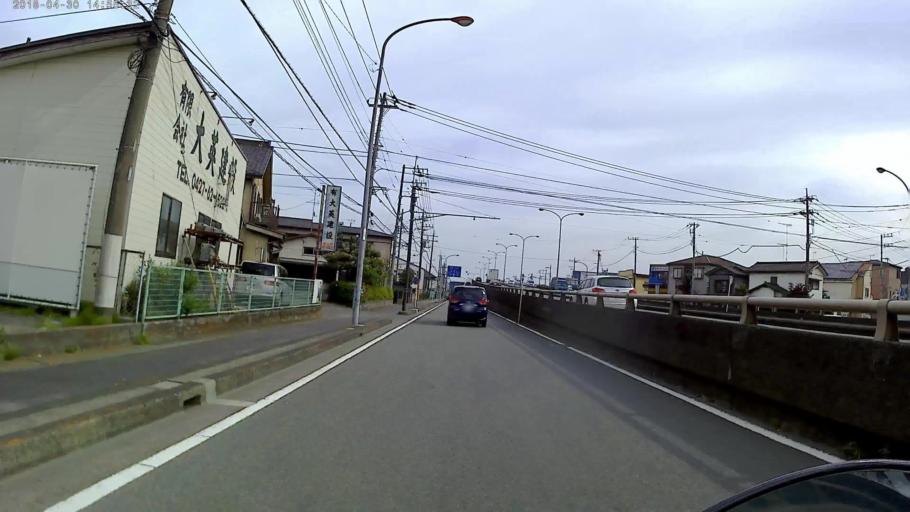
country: JP
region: Kanagawa
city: Zama
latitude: 35.5580
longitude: 139.3476
